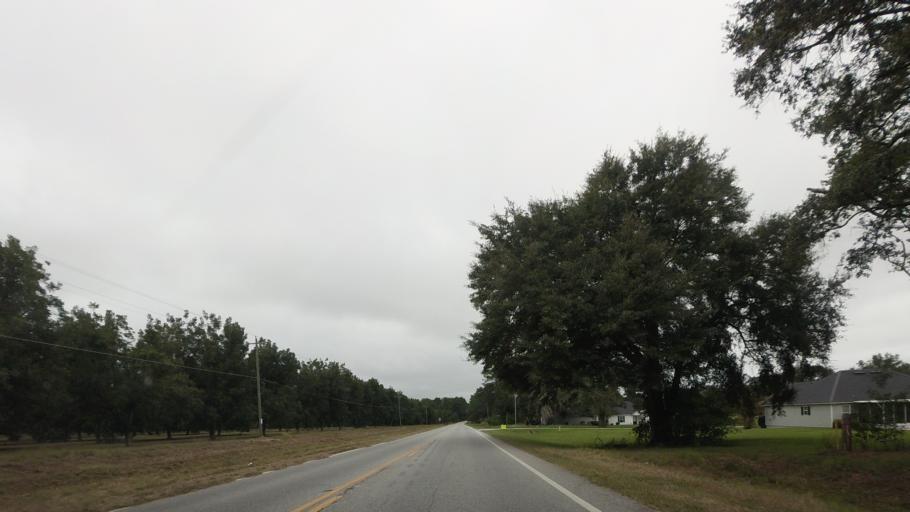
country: US
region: Georgia
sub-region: Berrien County
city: Ray City
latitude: 31.0451
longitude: -83.1978
